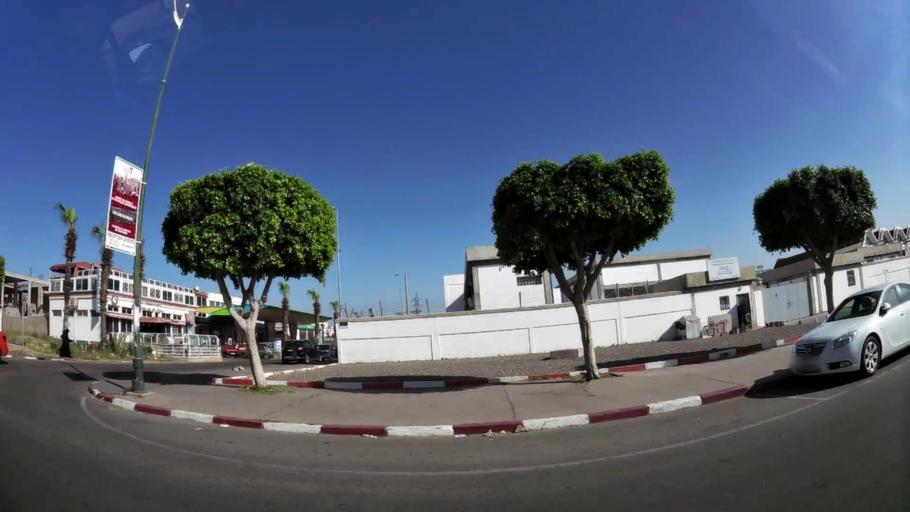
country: MA
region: Oued ed Dahab-Lagouira
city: Dakhla
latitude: 30.4159
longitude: -9.5674
